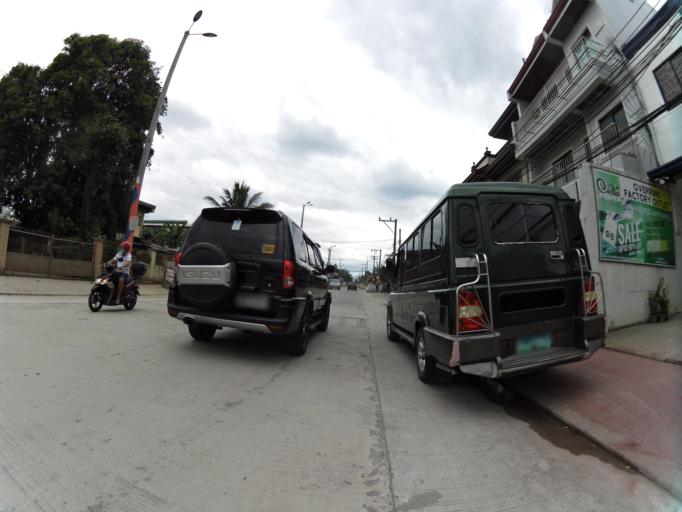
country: PH
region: Calabarzon
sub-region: Province of Rizal
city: Antipolo
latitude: 14.6383
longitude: 121.1092
